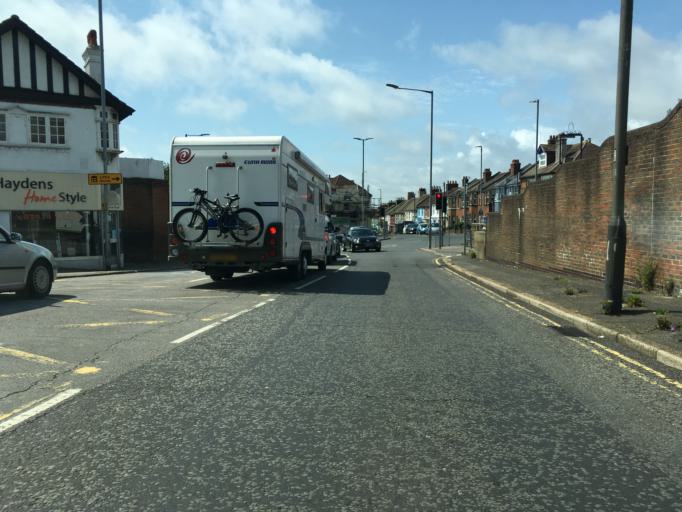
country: GB
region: England
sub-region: East Sussex
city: Hastings
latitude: 50.8688
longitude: 0.6017
